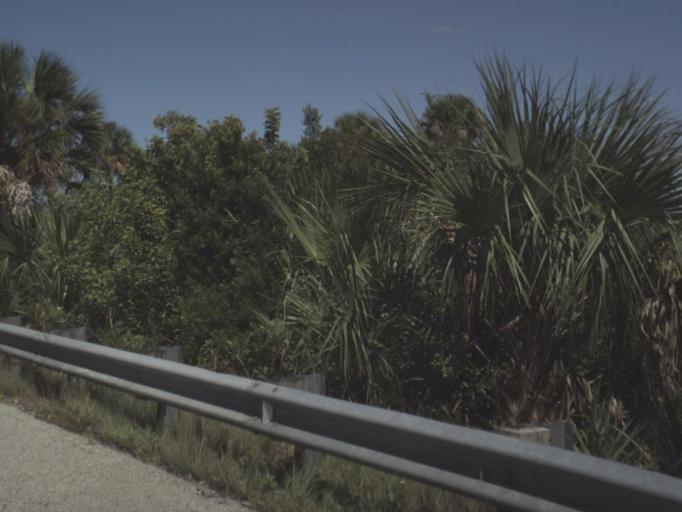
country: US
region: Florida
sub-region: Collier County
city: Marco
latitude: 25.9473
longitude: -81.4785
